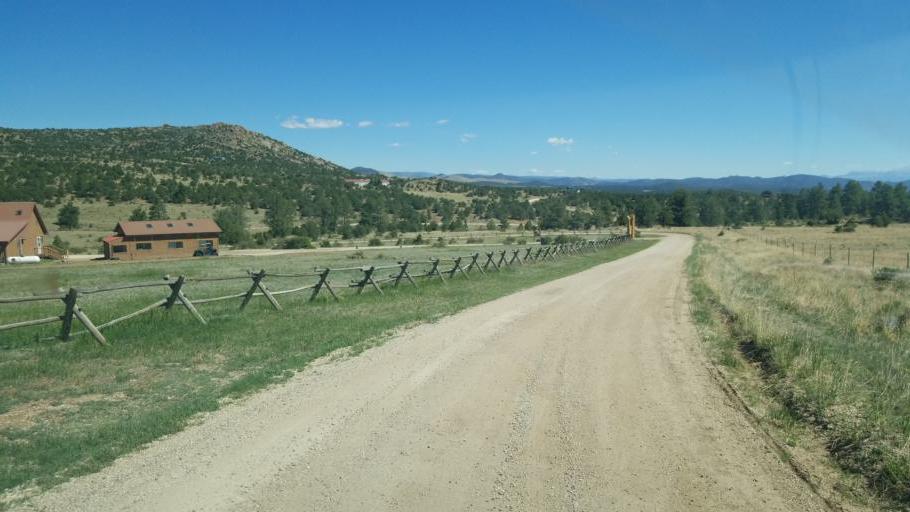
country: US
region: Colorado
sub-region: Custer County
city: Westcliffe
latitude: 38.2343
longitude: -105.4759
